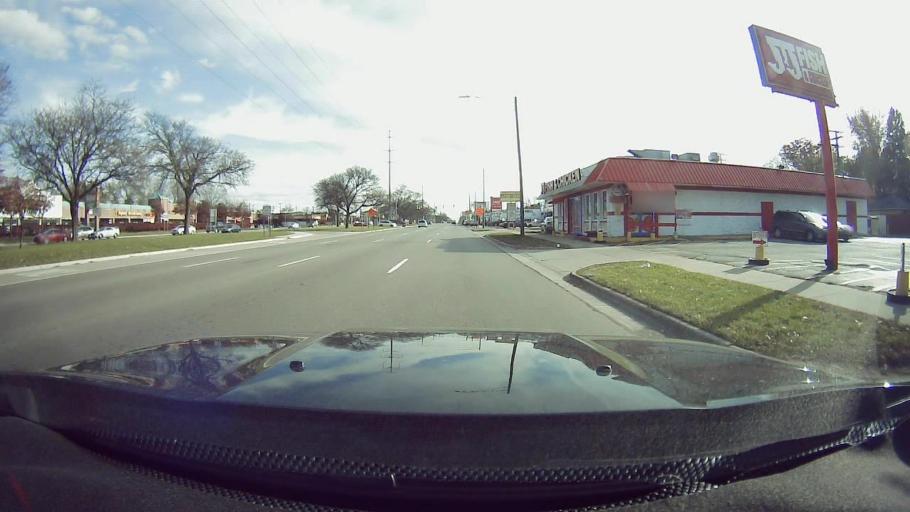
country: US
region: Michigan
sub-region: Oakland County
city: Southfield
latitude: 42.4436
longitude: -83.2429
